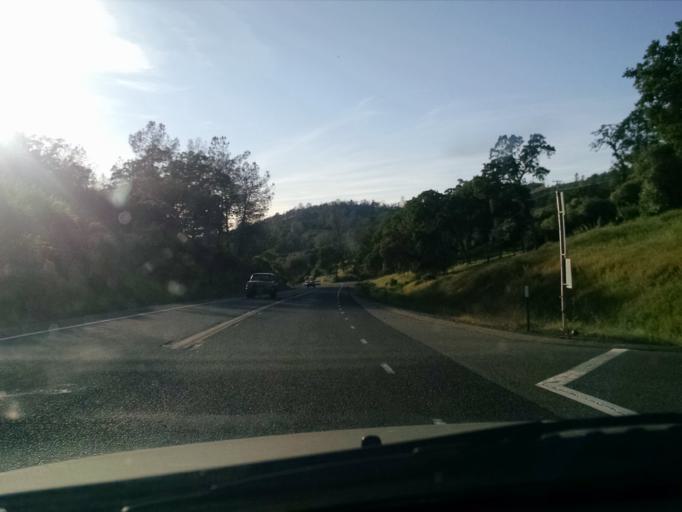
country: US
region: California
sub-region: Mariposa County
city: Mariposa
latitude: 37.4589
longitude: -119.9166
